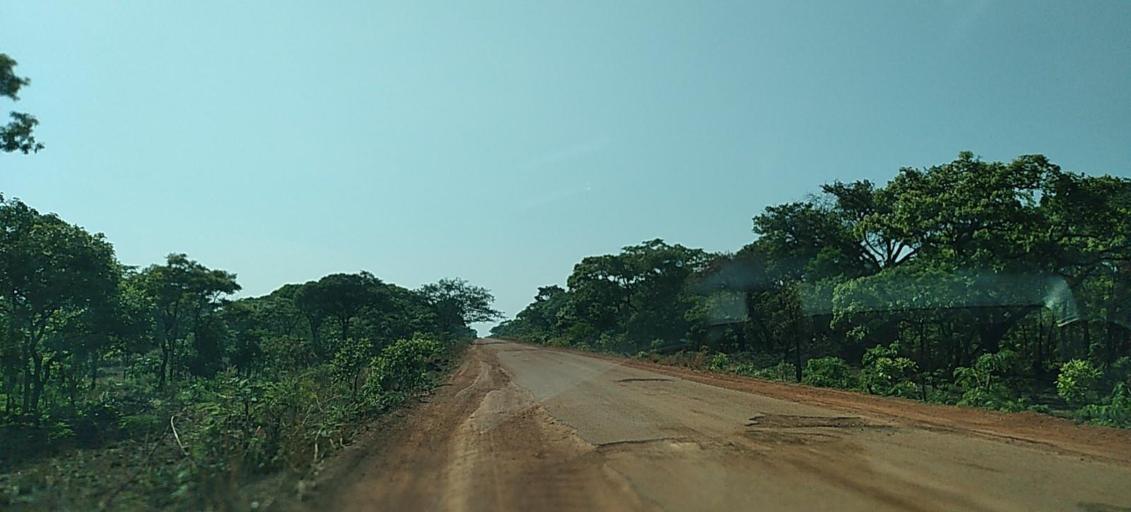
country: ZM
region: North-Western
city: Mwinilunga
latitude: -11.9068
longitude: 25.2904
